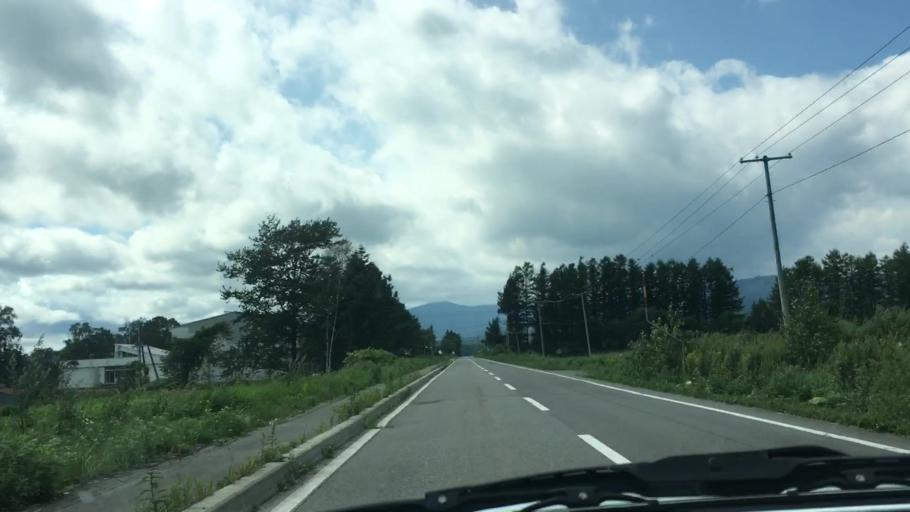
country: JP
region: Hokkaido
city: Otofuke
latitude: 43.2814
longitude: 143.3302
